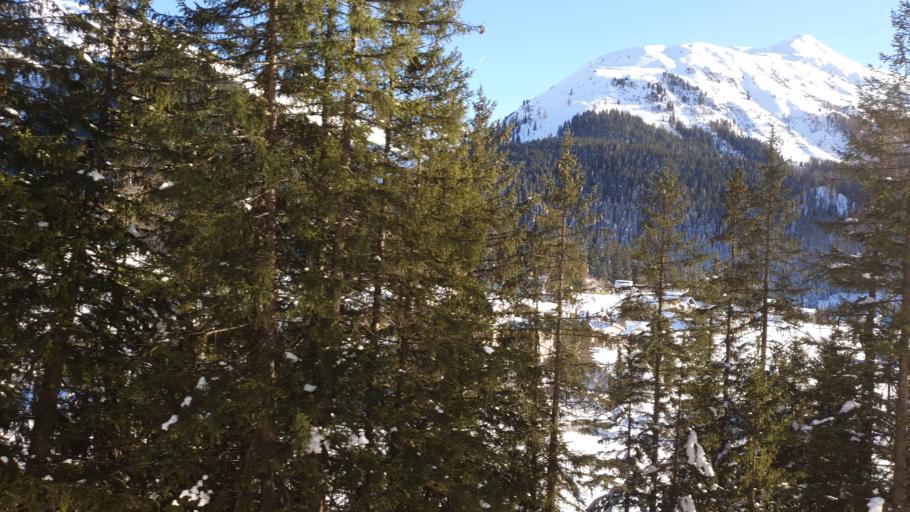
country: CH
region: Grisons
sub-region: Praettigau/Davos District
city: Davos
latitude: 46.8453
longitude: 9.8684
